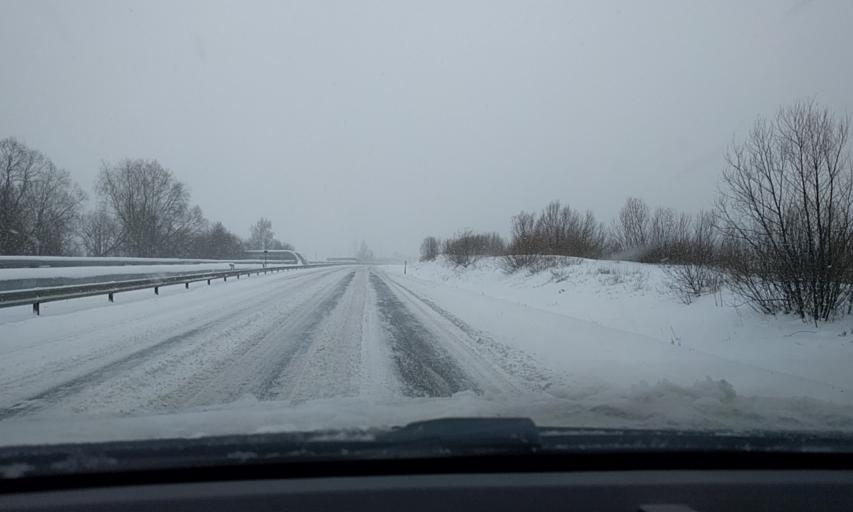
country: EE
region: Harju
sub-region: Maardu linn
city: Maardu
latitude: 59.4744
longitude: 24.9812
